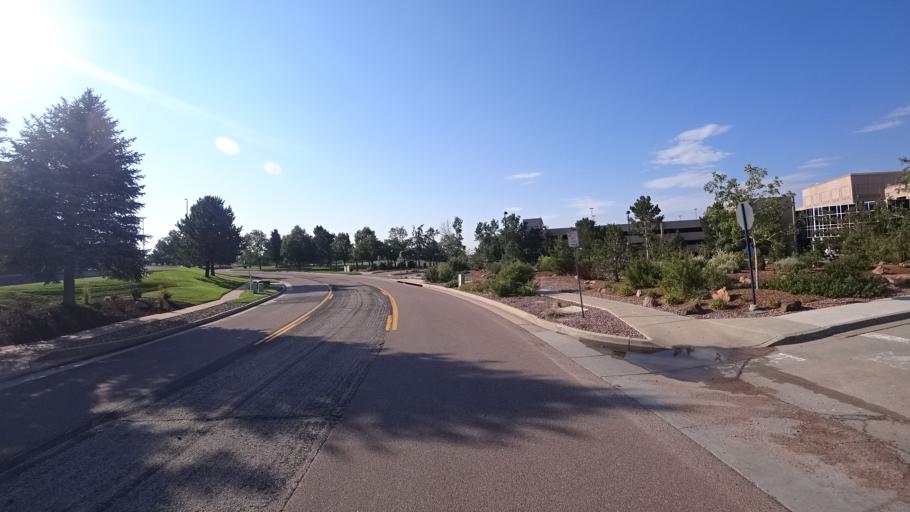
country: US
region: Colorado
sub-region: El Paso County
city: Air Force Academy
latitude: 38.9575
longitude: -104.7960
